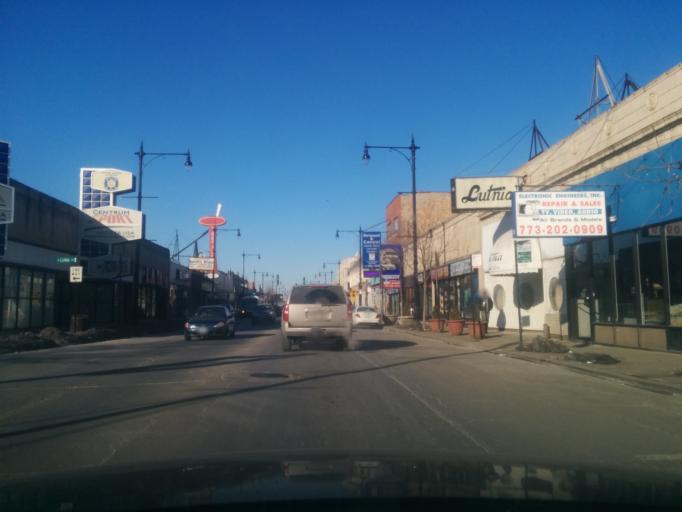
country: US
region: Illinois
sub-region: Cook County
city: Elmwood Park
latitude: 41.9386
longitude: -87.7651
